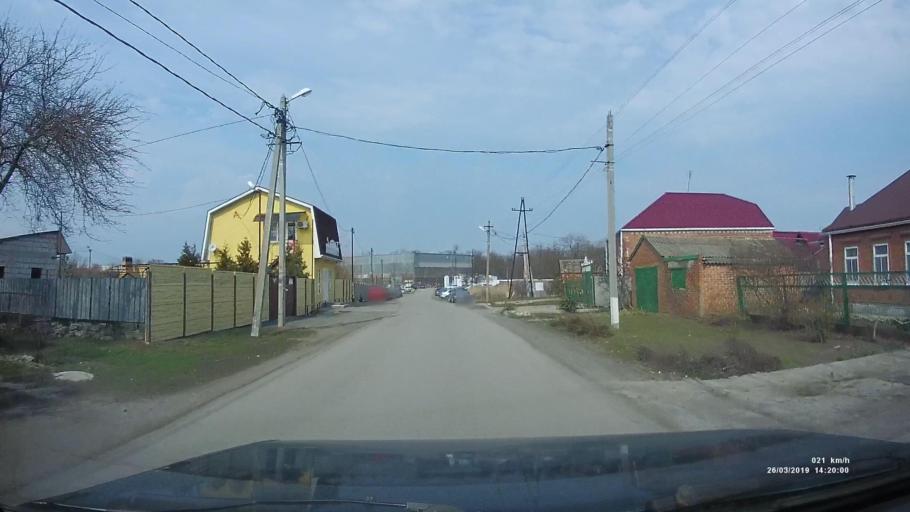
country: RU
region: Rostov
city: Novobessergenovka
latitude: 47.1900
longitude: 38.8707
